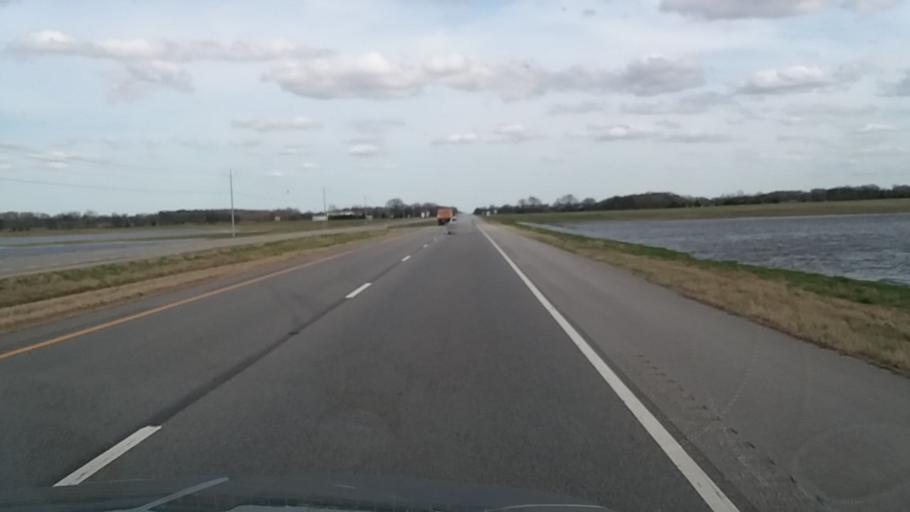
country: US
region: Alabama
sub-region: Lawrence County
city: Town Creek
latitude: 34.6838
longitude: -87.5281
